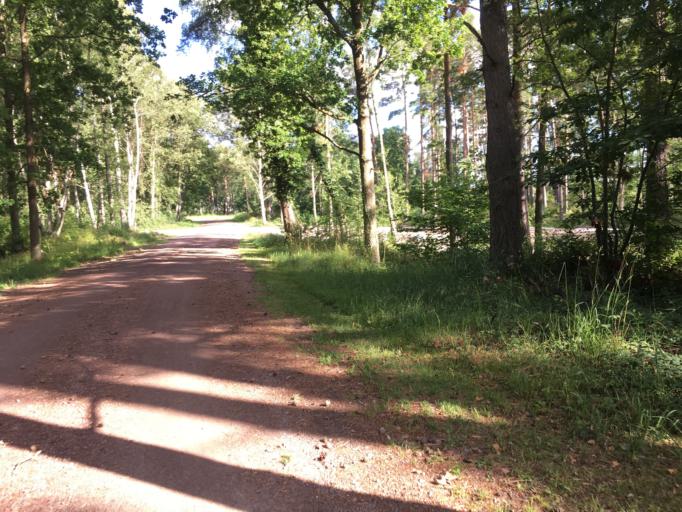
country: SE
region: Kalmar
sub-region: Kalmar Kommun
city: Kalmar
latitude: 56.6547
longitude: 16.3235
